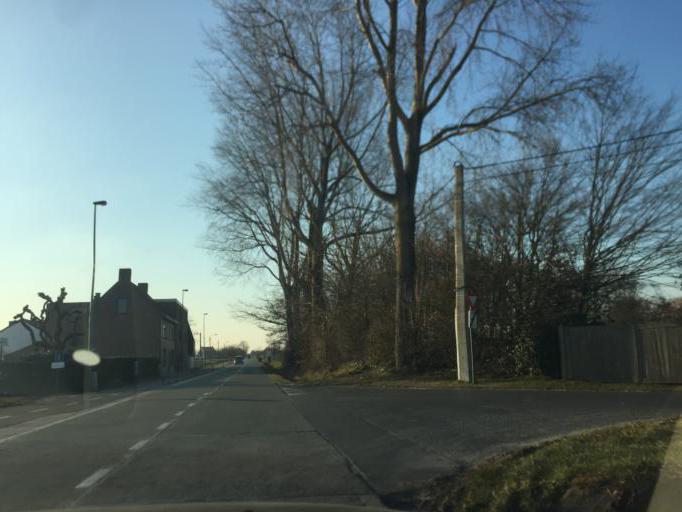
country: BE
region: Flanders
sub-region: Provincie West-Vlaanderen
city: Oostrozebeke
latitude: 50.9259
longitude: 3.3238
